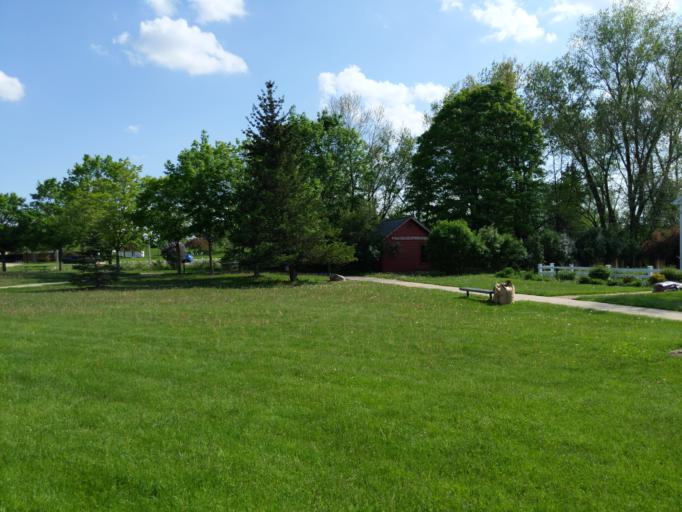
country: US
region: Michigan
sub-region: Ingham County
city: Okemos
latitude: 42.7301
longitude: -84.4152
